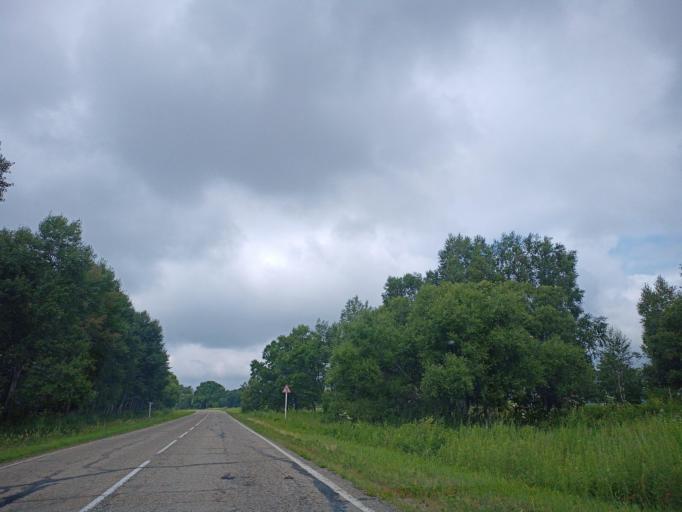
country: RU
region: Primorskiy
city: Dal'nerechensk
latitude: 45.9484
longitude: 133.9115
